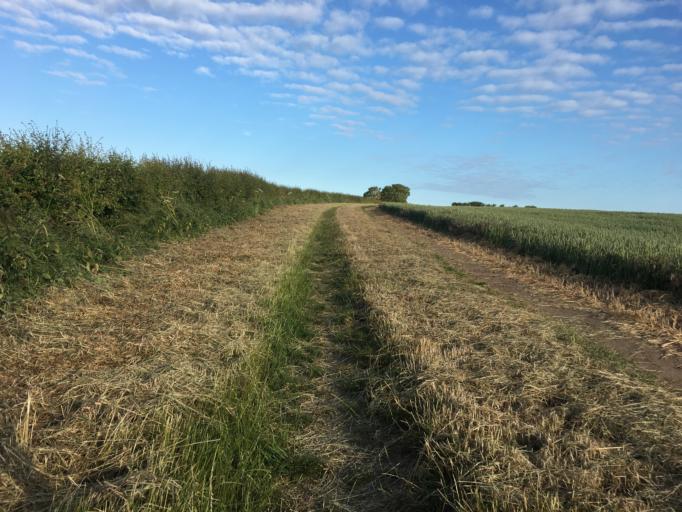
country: GB
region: England
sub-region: Northumberland
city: Bamburgh
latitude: 55.6013
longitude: -1.6990
